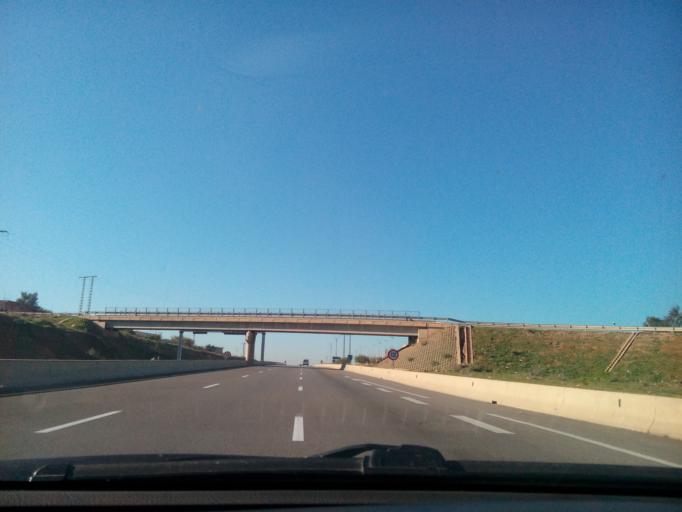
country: DZ
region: Chlef
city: Boukadir
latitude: 36.0536
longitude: 1.1347
